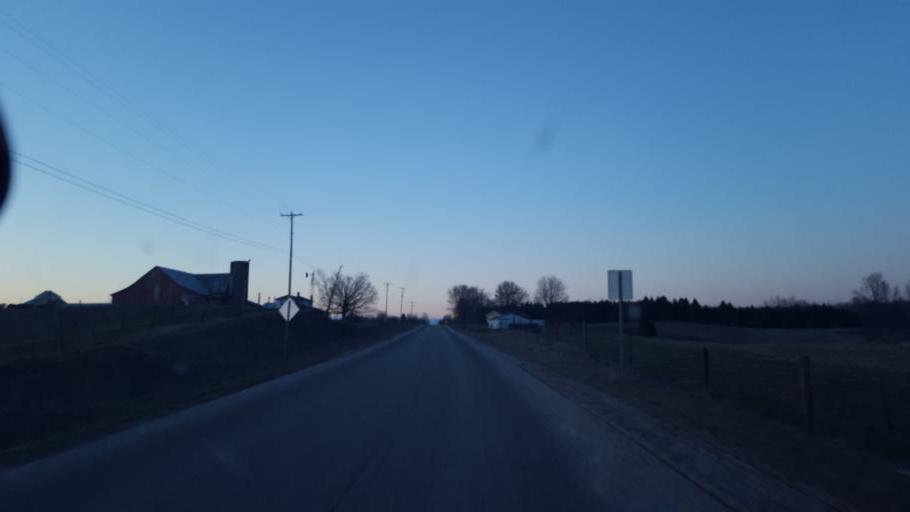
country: US
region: Michigan
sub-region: Montcalm County
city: Howard City
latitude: 43.5272
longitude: -85.4435
